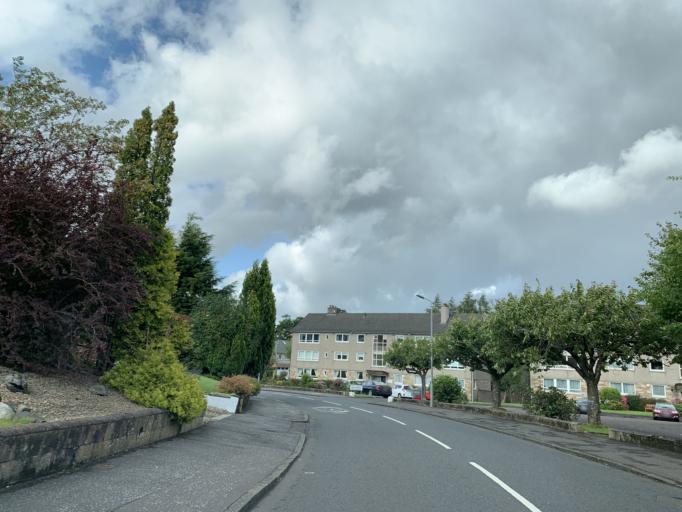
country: GB
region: Scotland
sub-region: East Renfrewshire
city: Newton Mearns
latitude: 55.7804
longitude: -4.3243
